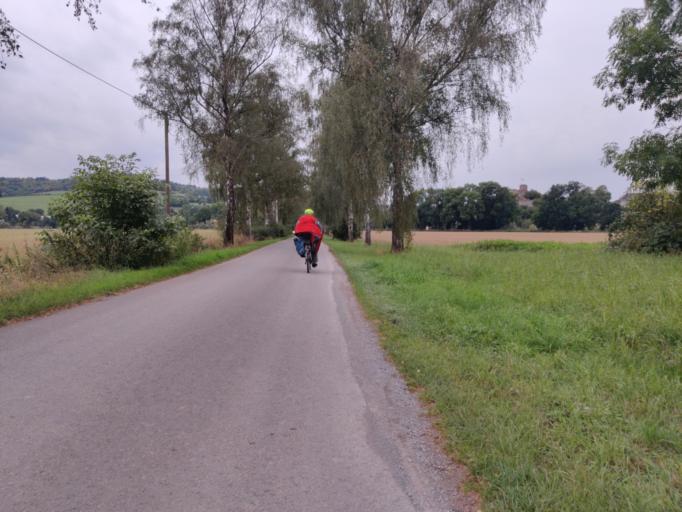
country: DE
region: Lower Saxony
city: Polle
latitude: 51.8982
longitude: 9.4142
